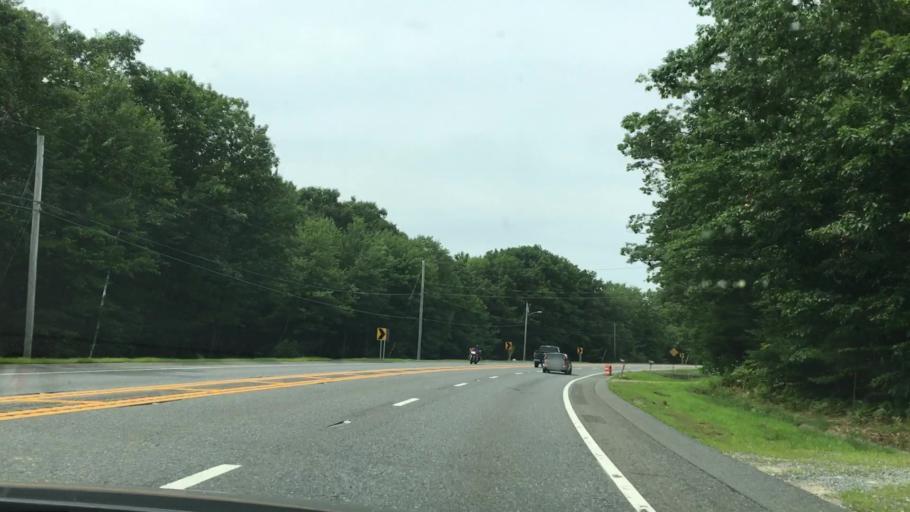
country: US
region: Massachusetts
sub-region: Worcester County
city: Gardner
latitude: 42.6177
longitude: -72.0076
